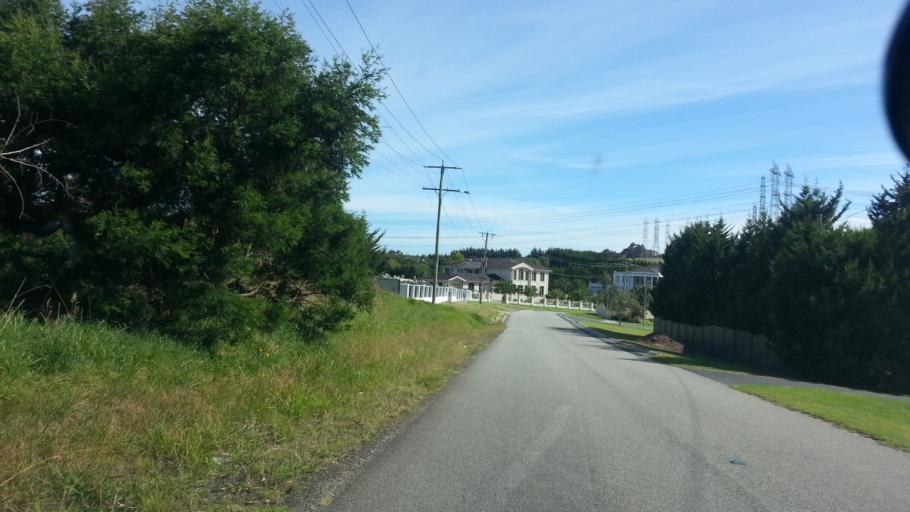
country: AU
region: Victoria
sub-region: Casey
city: Endeavour Hills
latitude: -37.9770
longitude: 145.2860
